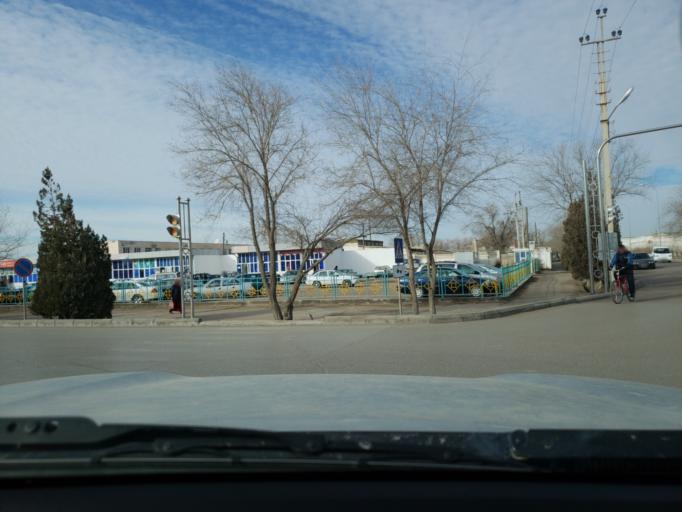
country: TM
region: Dasoguz
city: Dasoguz
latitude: 41.8498
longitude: 59.9662
